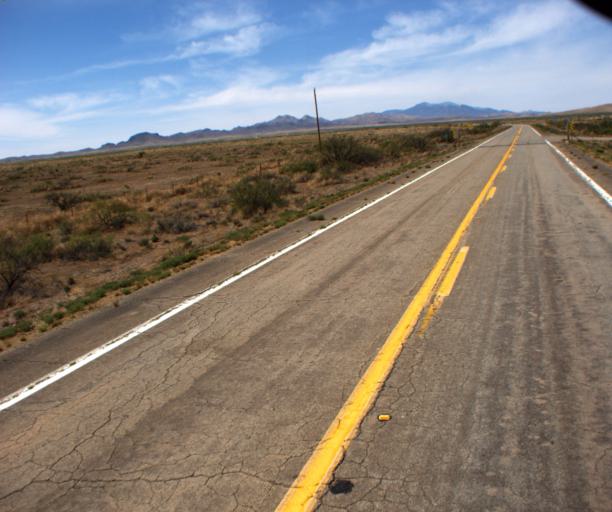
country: US
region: Arizona
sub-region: Cochise County
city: Willcox
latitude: 32.3649
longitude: -109.6222
